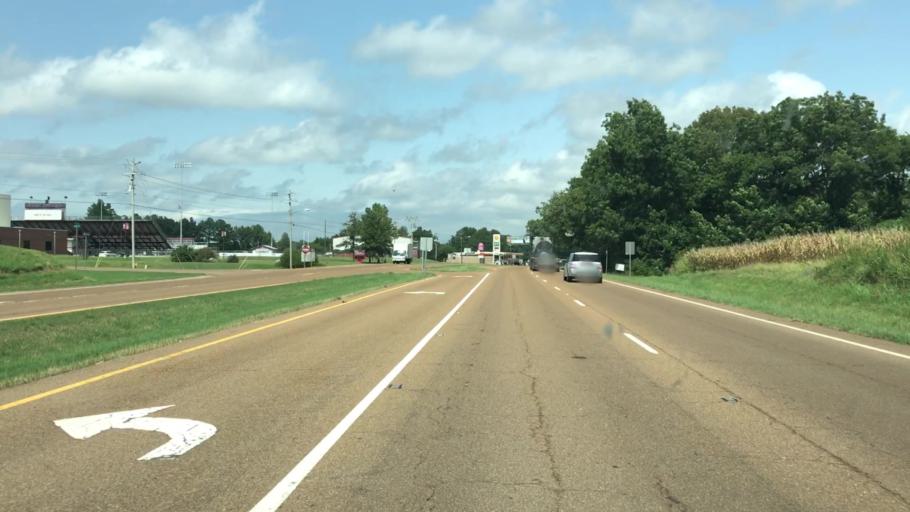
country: US
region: Tennessee
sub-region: Obion County
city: Troy
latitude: 36.3419
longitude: -89.1545
